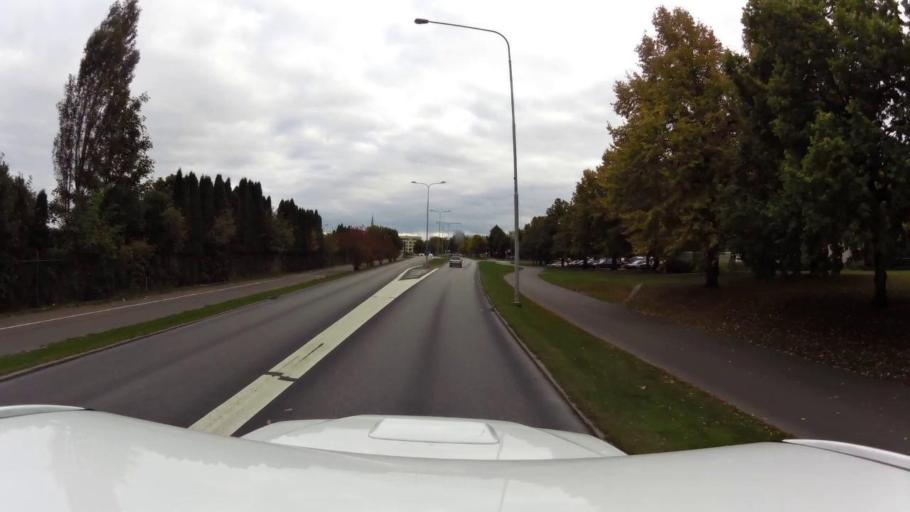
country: SE
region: OEstergoetland
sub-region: Linkopings Kommun
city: Linkoping
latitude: 58.4171
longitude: 15.6014
